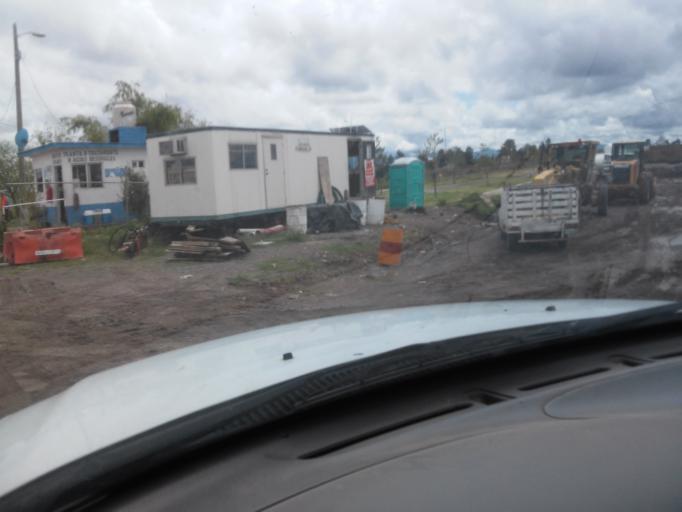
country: MX
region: Durango
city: Victoria de Durango
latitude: 24.0256
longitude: -104.6140
